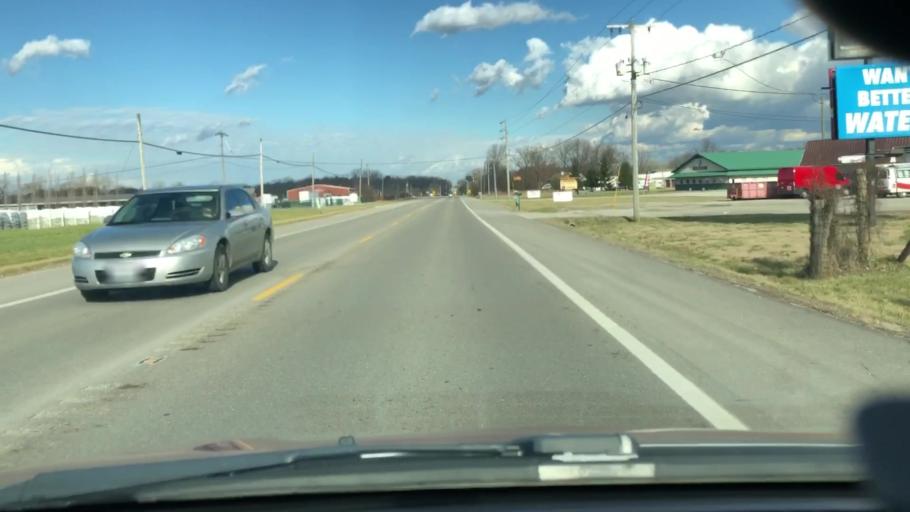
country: US
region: Ohio
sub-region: Clark County
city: Springfield
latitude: 39.8686
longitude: -83.8465
